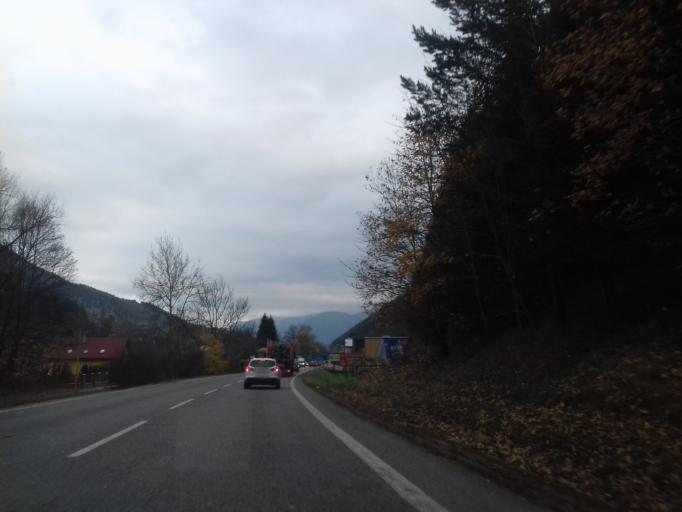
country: SK
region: Zilinsky
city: Ruzomberok
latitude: 49.0230
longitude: 19.2926
